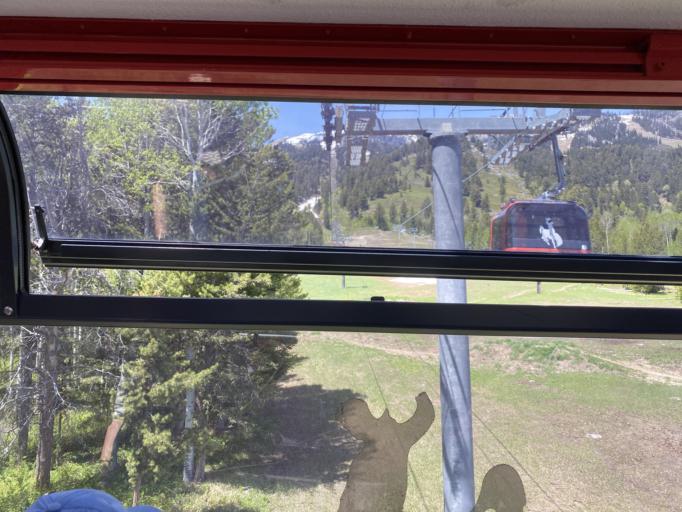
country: US
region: Wyoming
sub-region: Teton County
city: Moose Wilson Road
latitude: 43.5898
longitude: -110.8306
